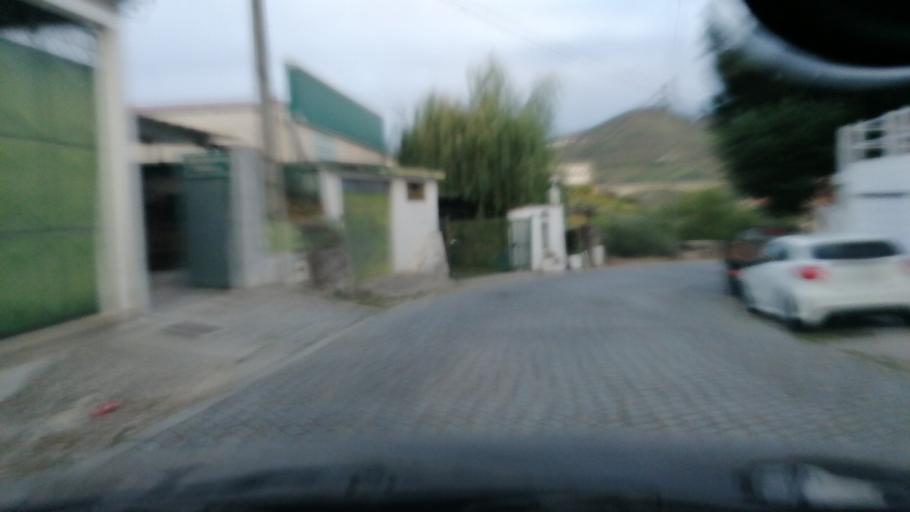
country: PT
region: Vila Real
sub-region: Peso da Regua
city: Peso da Regua
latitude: 41.1611
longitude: -7.7842
